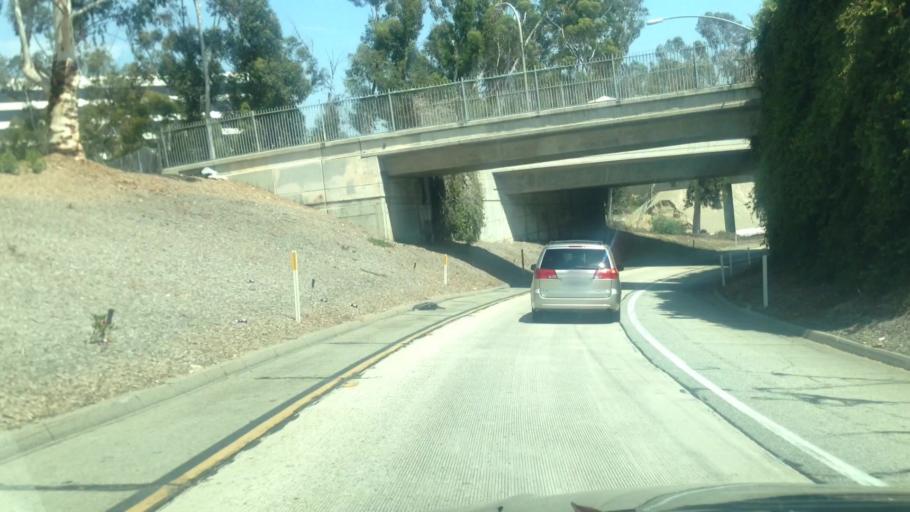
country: US
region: California
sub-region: Los Angeles County
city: Pasadena
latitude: 34.1474
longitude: -118.1566
